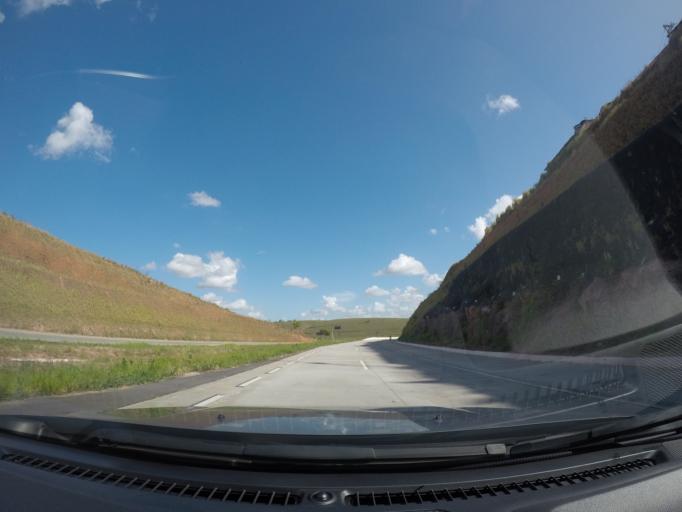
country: BR
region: Alagoas
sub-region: Novo Lino
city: Novo Lino
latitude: -8.8029
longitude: -35.6233
